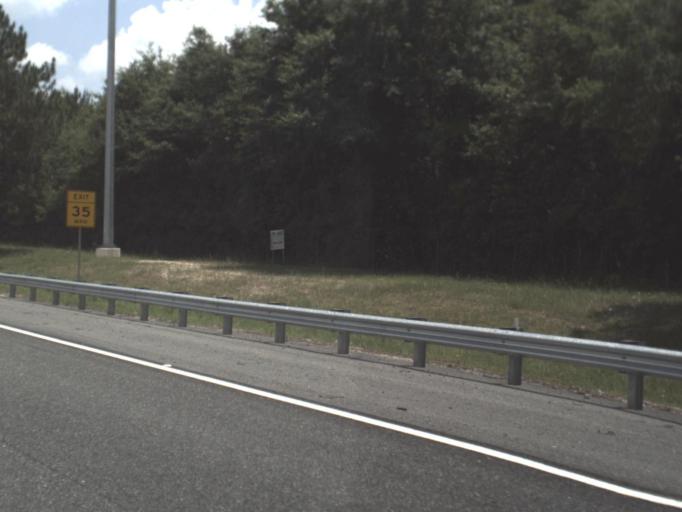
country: US
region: Florida
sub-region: Hamilton County
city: Jasper
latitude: 30.5201
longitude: -83.0619
